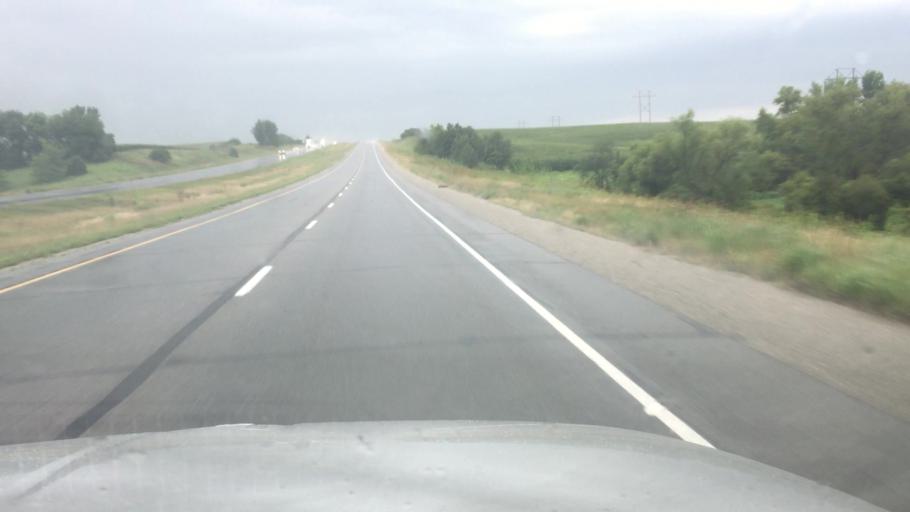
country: US
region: Iowa
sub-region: Washington County
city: Washington
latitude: 41.3645
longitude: -91.5518
